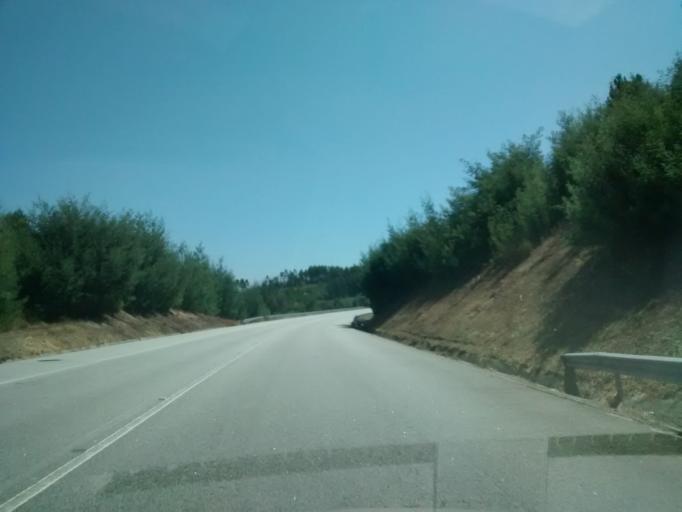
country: PT
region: Coimbra
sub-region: Tabua
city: Tabua
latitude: 40.3730
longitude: -8.0267
